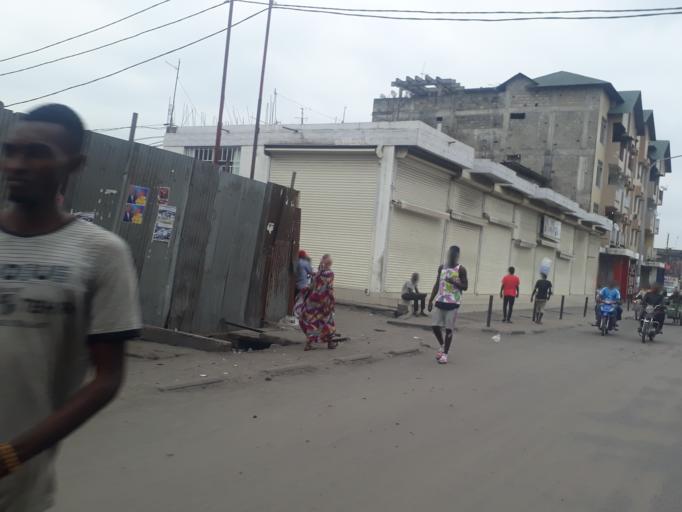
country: CD
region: Kinshasa
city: Kinshasa
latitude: -4.3153
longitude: 15.3100
